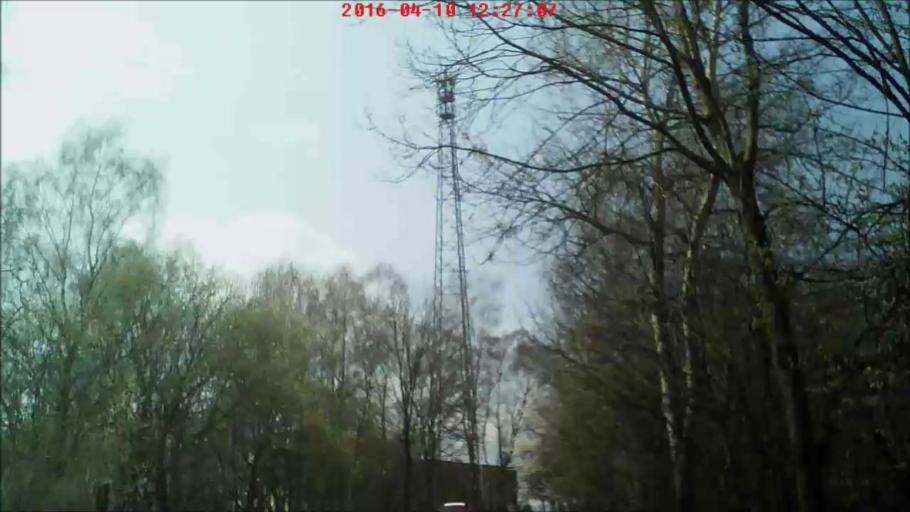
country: DE
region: Thuringia
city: Steinbach-Hallenberg
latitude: 50.6850
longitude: 10.5493
